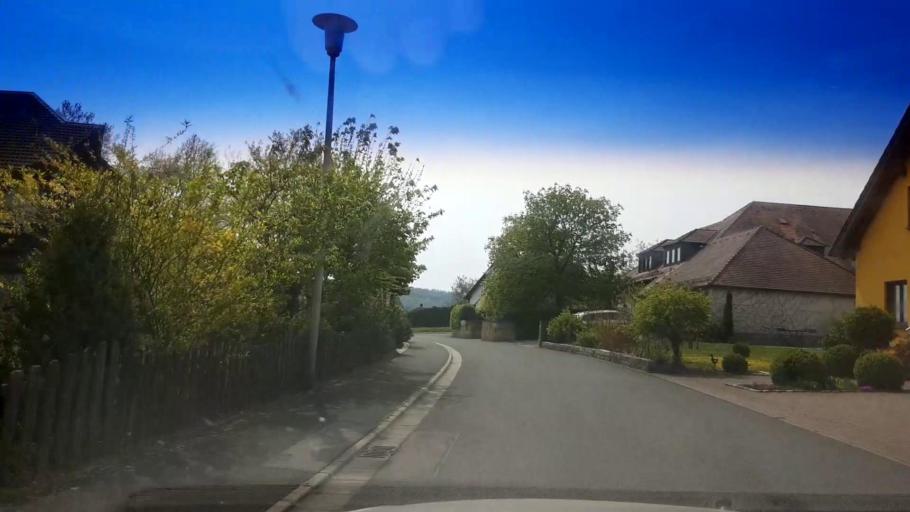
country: DE
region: Bavaria
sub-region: Upper Franconia
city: Baunach
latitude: 49.9867
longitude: 10.8403
